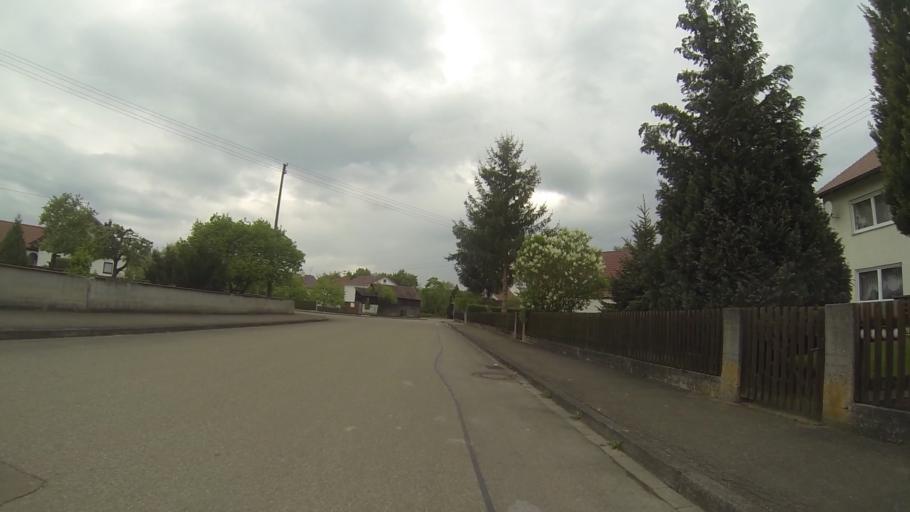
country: DE
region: Bavaria
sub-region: Swabia
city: Wittislingen
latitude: 48.6220
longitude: 10.4194
